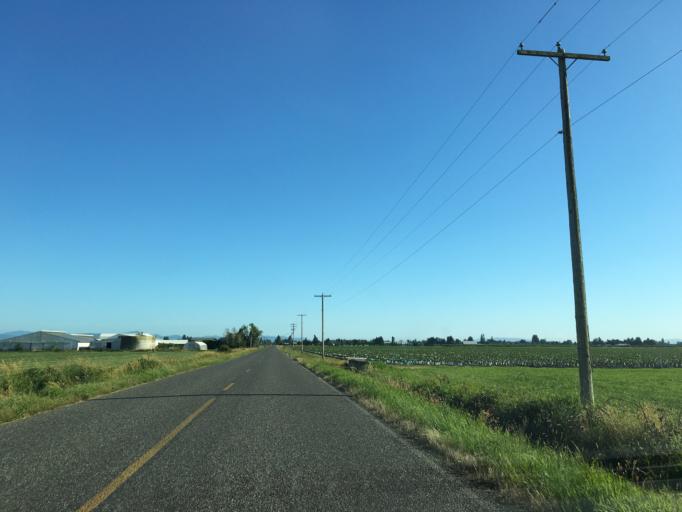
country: US
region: Washington
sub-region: Whatcom County
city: Lynden
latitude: 48.9779
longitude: -122.4519
